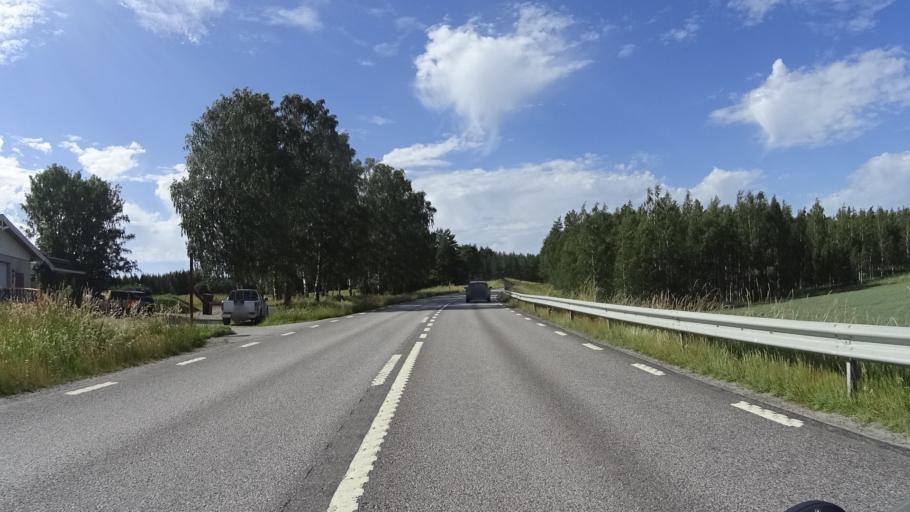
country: SE
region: OEstergoetland
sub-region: Linkopings Kommun
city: Sturefors
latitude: 58.3226
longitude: 15.8627
